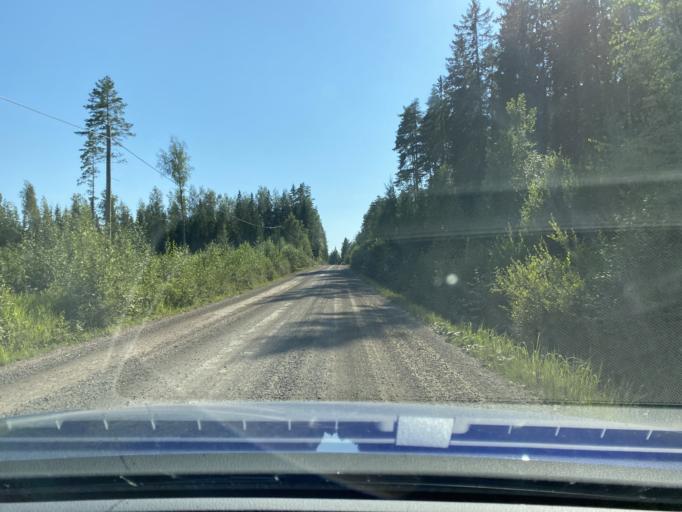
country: FI
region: Satakunta
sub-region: Rauma
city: Kiukainen
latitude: 61.1388
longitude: 21.9927
